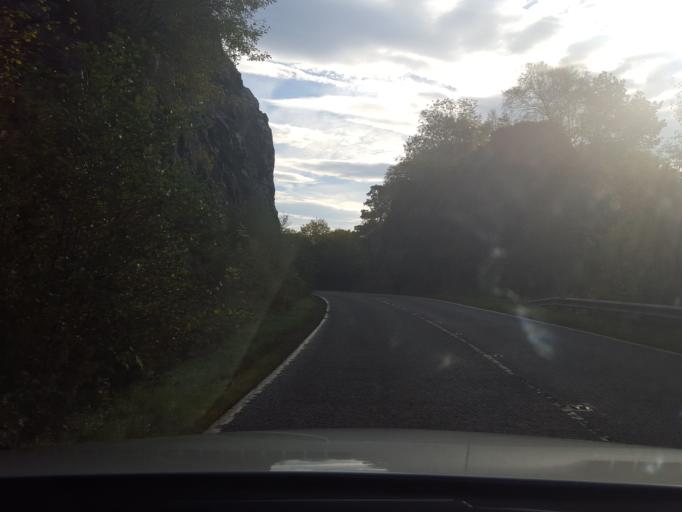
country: GB
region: Scotland
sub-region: Highland
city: Fort William
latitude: 57.2592
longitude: -5.4906
